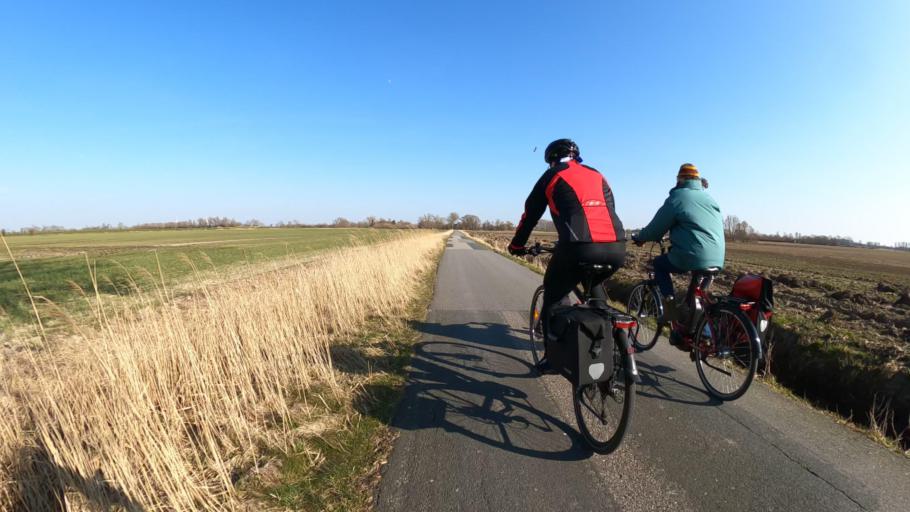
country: DE
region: Schleswig-Holstein
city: Seestermuhe
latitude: 53.7124
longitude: 9.5433
